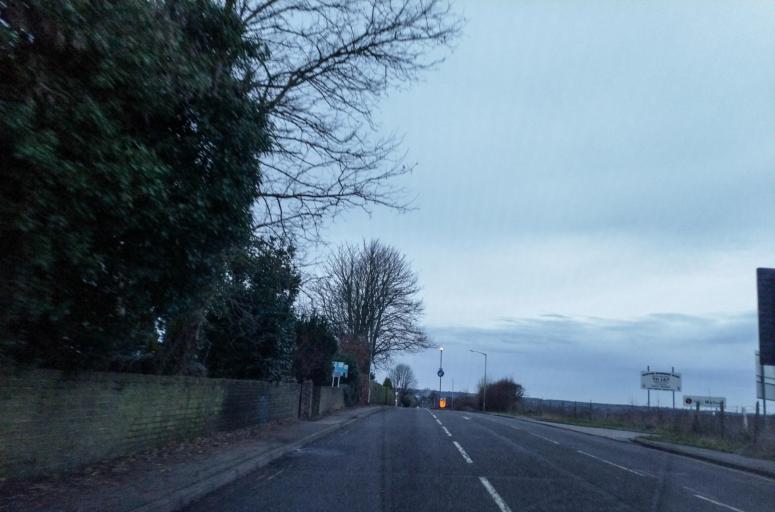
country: GB
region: England
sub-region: Kent
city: Canterbury
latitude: 51.2631
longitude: 1.1021
